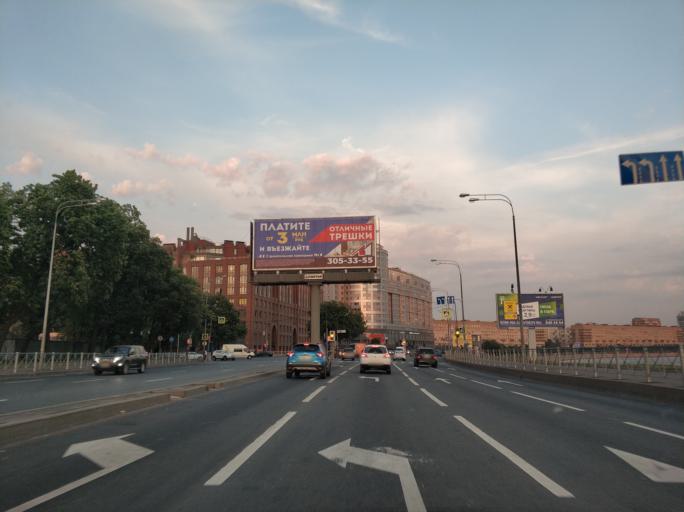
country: RU
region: Leningrad
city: Finlyandskiy
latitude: 59.9580
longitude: 30.4020
